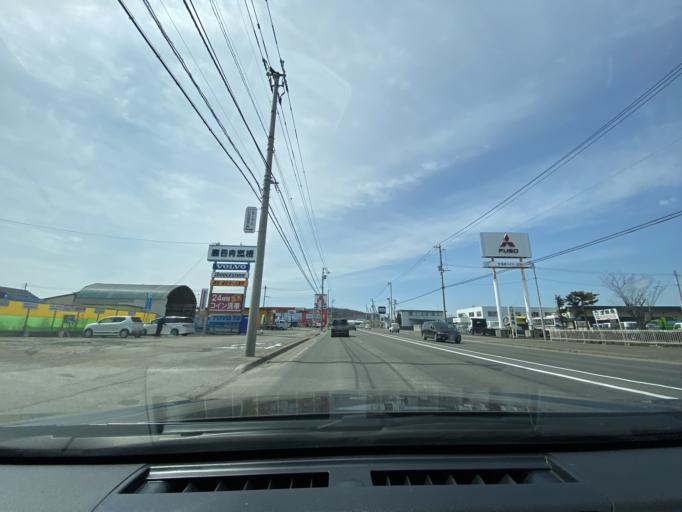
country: JP
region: Hokkaido
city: Kitami
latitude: 43.7968
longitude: 143.8409
